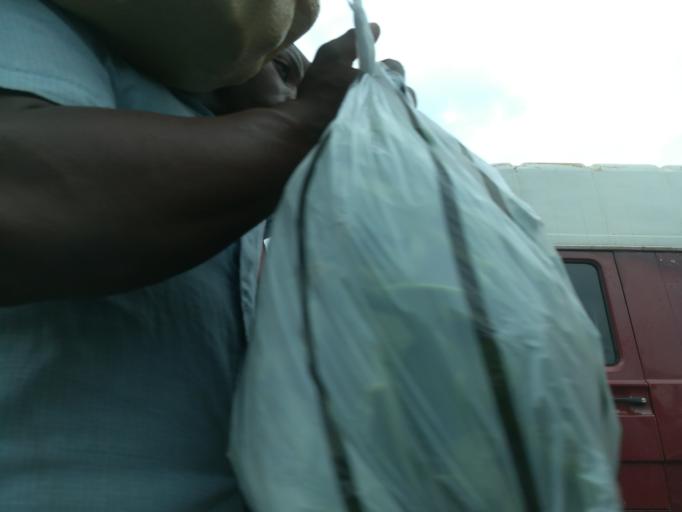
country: NG
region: Lagos
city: Ojota
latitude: 6.6095
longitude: 3.3960
